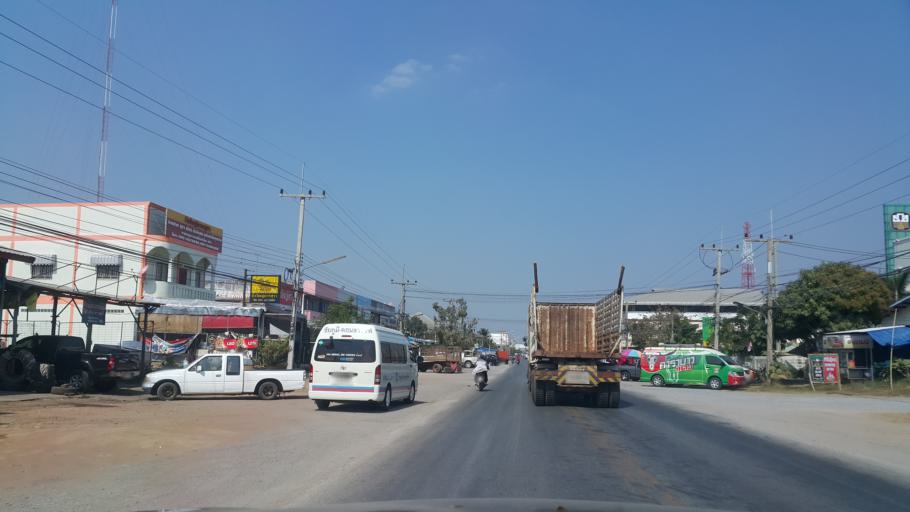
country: TH
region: Chaiyaphum
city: Khon Sawan
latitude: 15.9234
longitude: 102.2795
